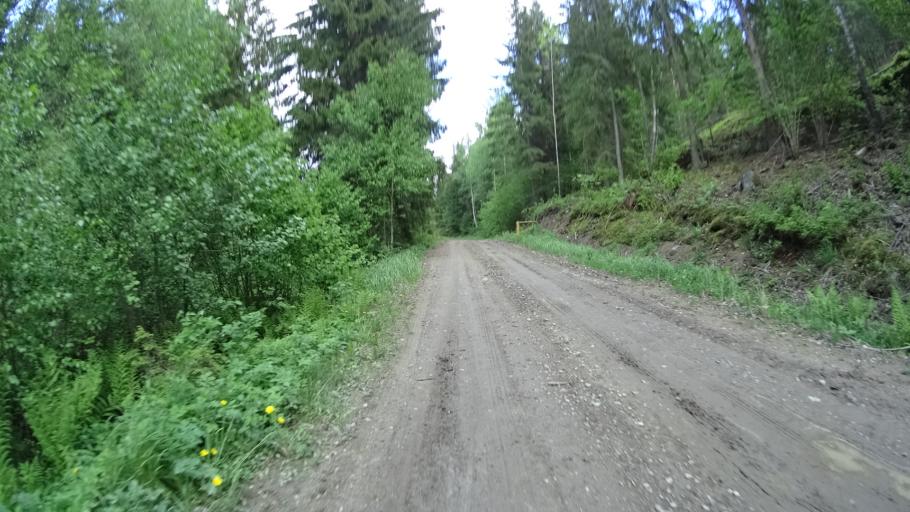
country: FI
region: Uusimaa
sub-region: Raaseporin
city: Karis
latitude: 60.1494
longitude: 23.6243
